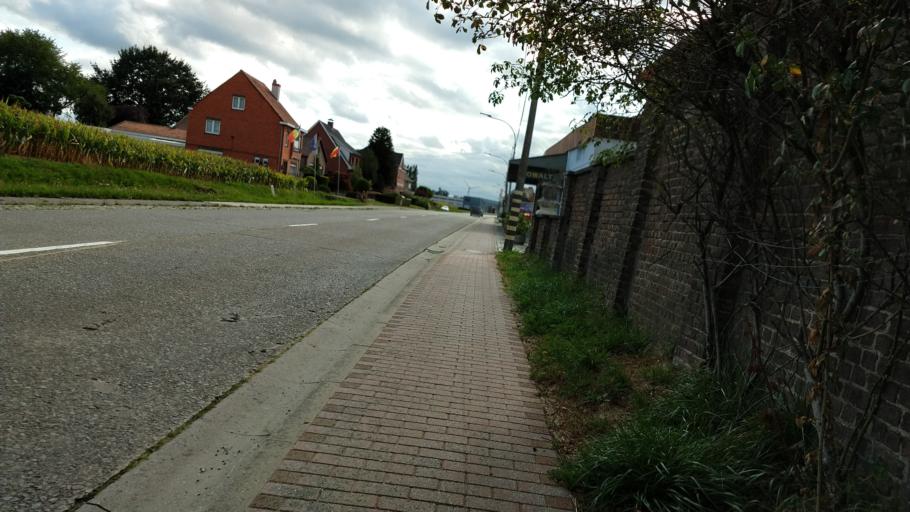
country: BE
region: Flanders
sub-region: Provincie Oost-Vlaanderen
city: Wetteren
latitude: 50.9963
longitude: 3.8503
